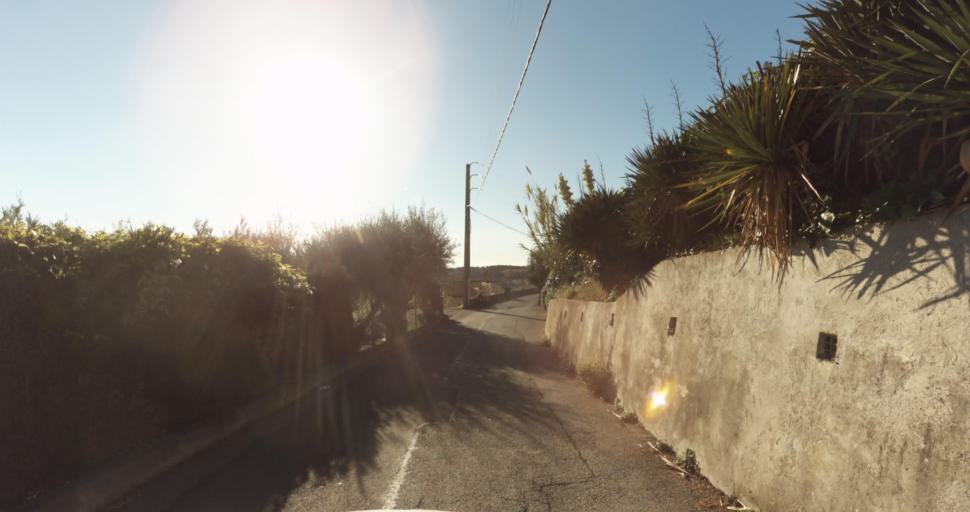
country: FR
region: Provence-Alpes-Cote d'Azur
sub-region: Departement des Alpes-Maritimes
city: Vence
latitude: 43.7287
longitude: 7.0851
